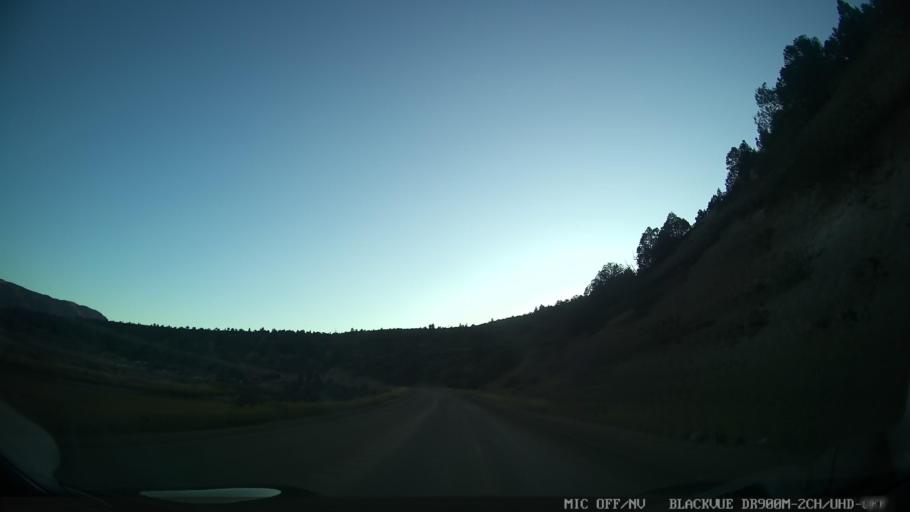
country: US
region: Colorado
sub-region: Eagle County
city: Edwards
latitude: 39.8914
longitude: -106.6129
